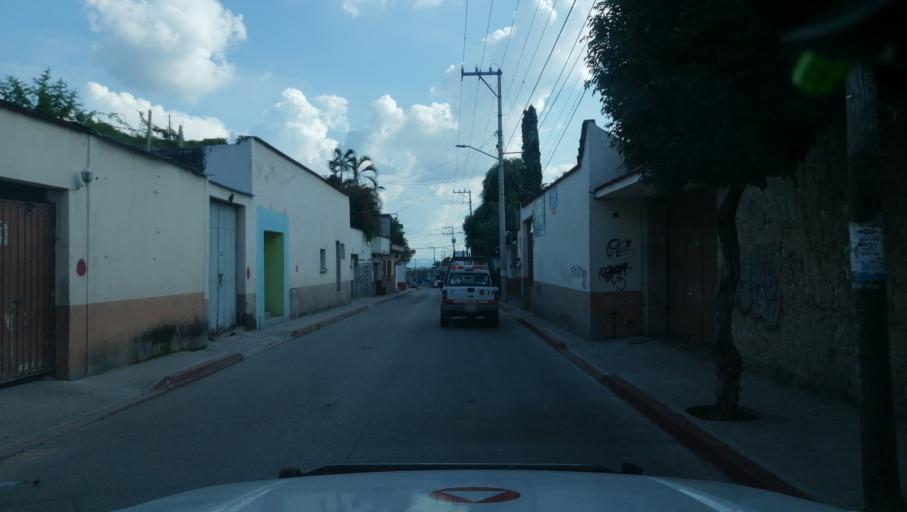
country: MX
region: Morelos
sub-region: Ayala
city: Ciudad Ayala
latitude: 18.7633
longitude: -98.9839
